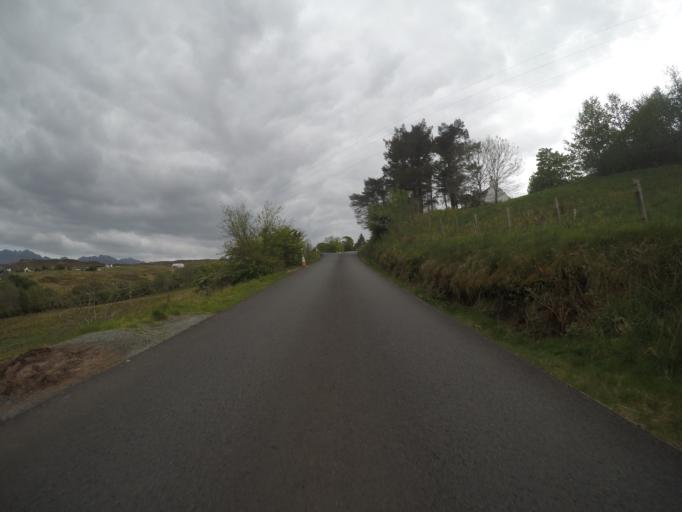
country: GB
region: Scotland
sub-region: Highland
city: Isle of Skye
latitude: 57.3016
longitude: -6.3578
